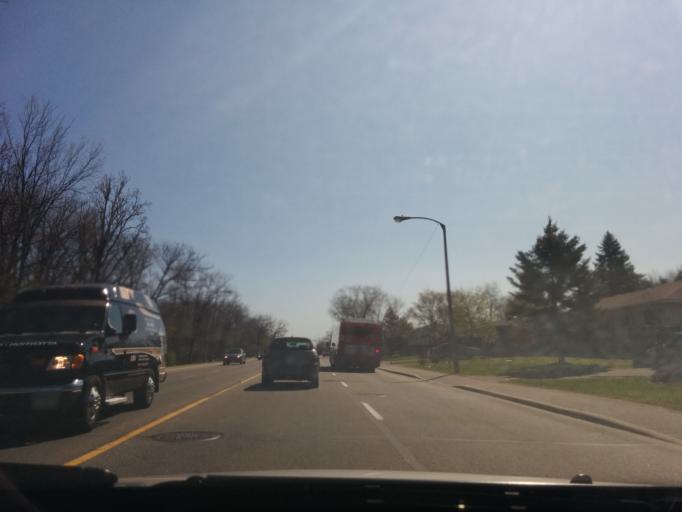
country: CA
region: Ontario
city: Ottawa
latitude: 45.3991
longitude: -75.6513
